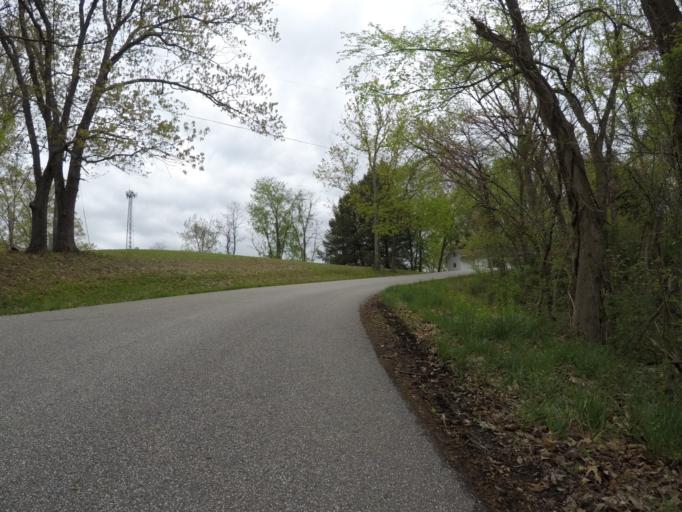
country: US
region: West Virginia
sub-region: Cabell County
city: Barboursville
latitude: 38.4035
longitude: -82.2712
